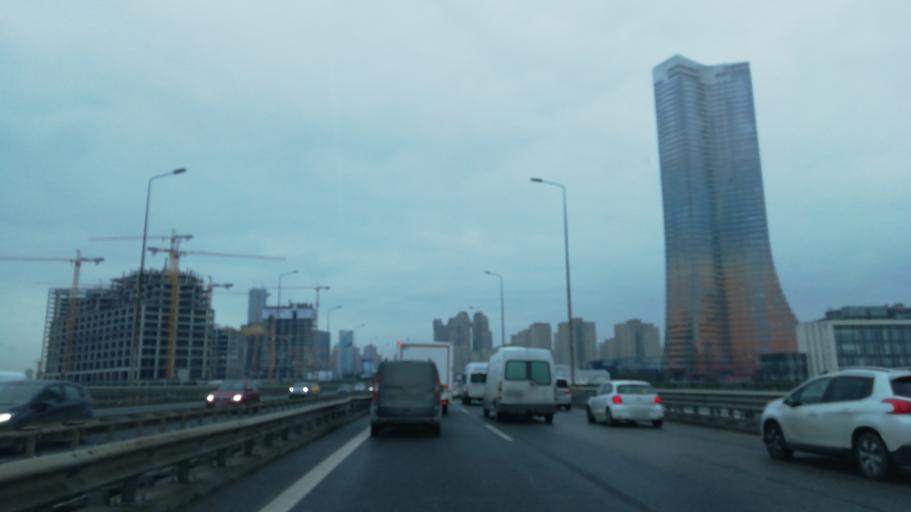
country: TR
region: Istanbul
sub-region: Atasehir
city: Atasehir
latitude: 41.0043
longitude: 29.1015
